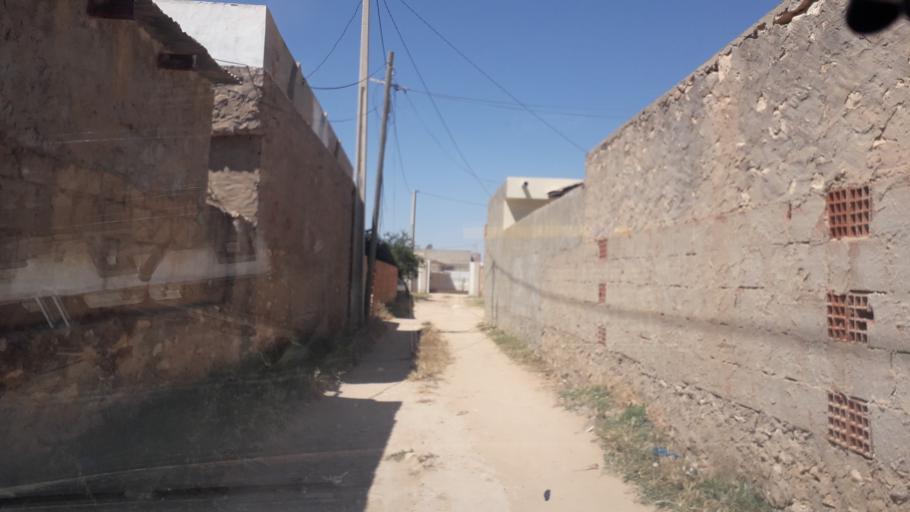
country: TN
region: Safaqis
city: Al Qarmadah
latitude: 34.8307
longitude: 10.7674
